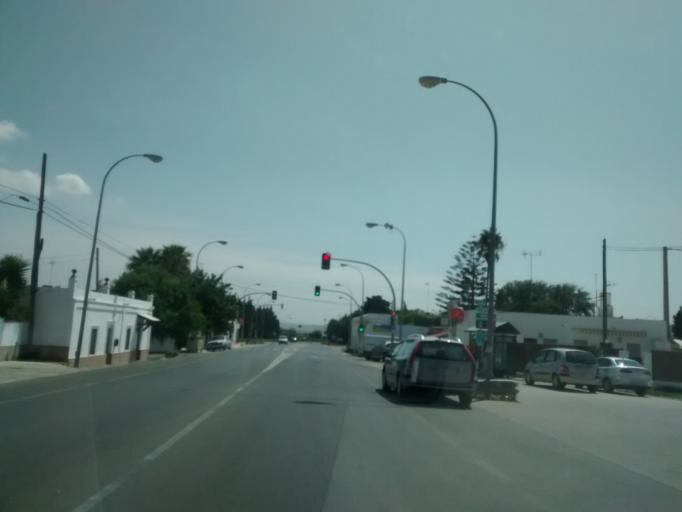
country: ES
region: Andalusia
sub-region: Provincia de Cadiz
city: Conil de la Frontera
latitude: 36.2953
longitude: -6.0742
